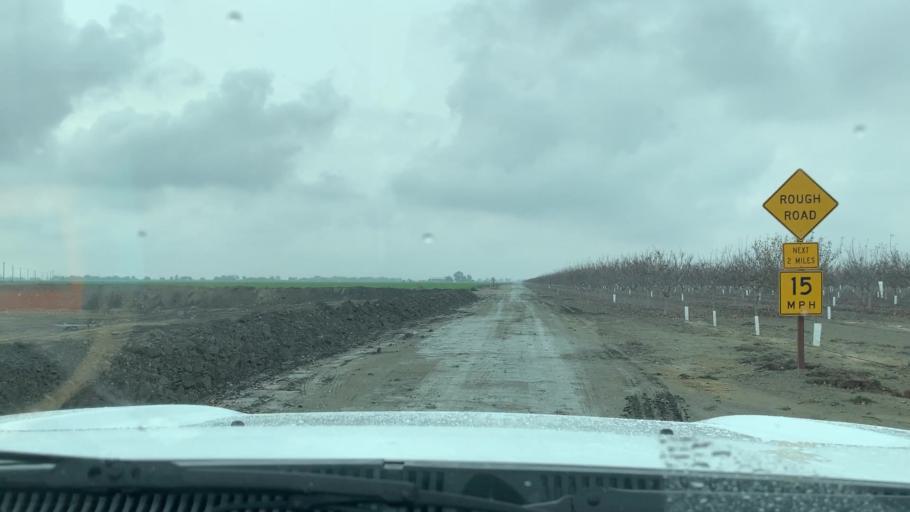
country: US
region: California
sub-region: Kings County
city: Corcoran
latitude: 36.0224
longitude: -119.5005
